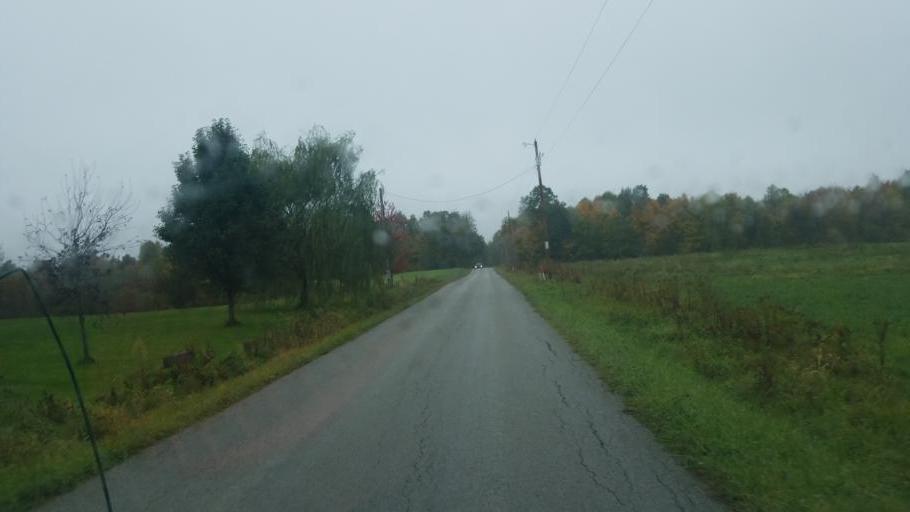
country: US
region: Ohio
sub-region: Morrow County
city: Mount Gilead
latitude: 40.5825
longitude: -82.7121
